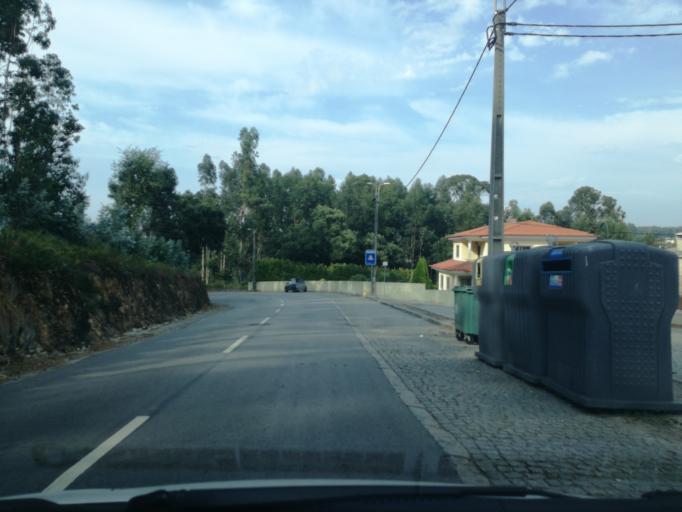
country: PT
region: Porto
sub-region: Vila Nova de Gaia
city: Sao Felix da Marinha
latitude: 41.0286
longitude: -8.6293
